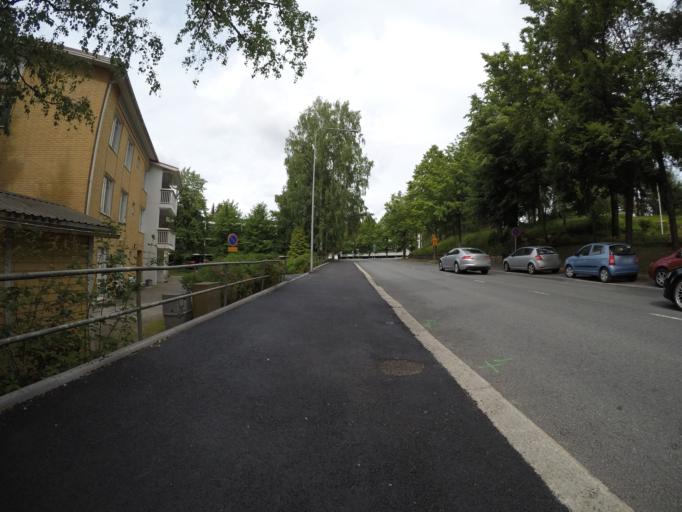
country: FI
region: Haeme
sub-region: Haemeenlinna
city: Haemeenlinna
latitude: 61.0035
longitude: 24.4841
